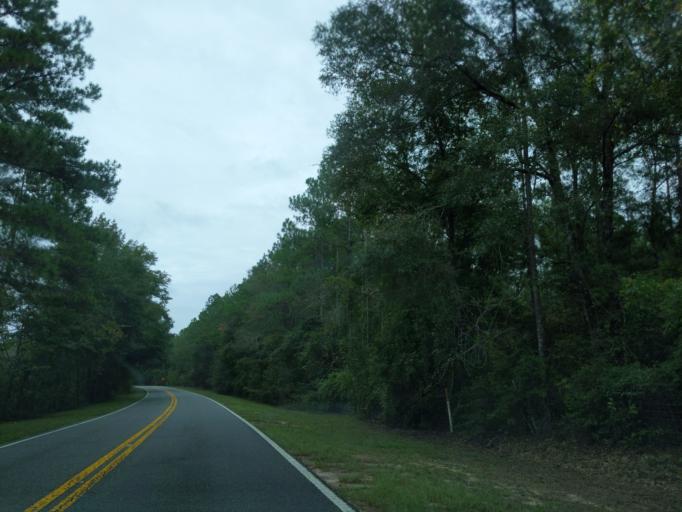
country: US
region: Florida
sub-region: Leon County
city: Woodville
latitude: 30.3670
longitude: -84.1513
